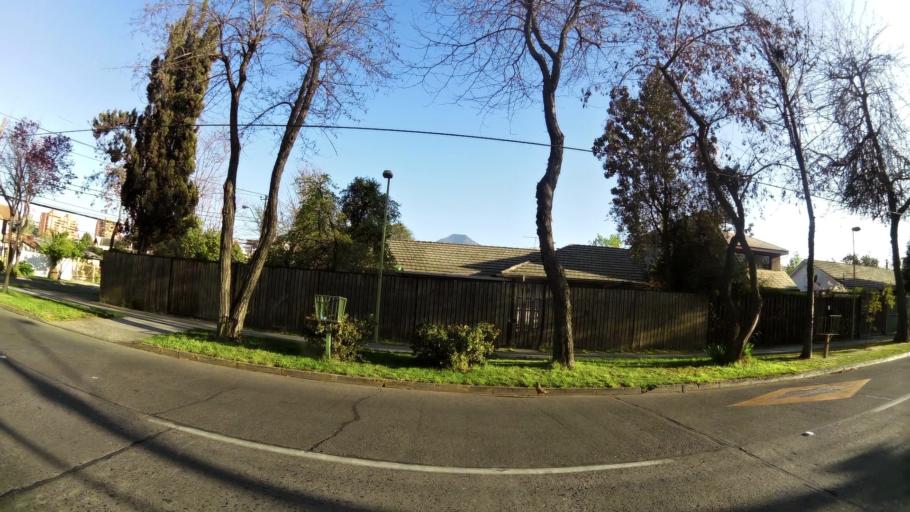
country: CL
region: Santiago Metropolitan
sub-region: Provincia de Santiago
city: Villa Presidente Frei, Nunoa, Santiago, Chile
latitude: -33.3990
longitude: -70.5598
